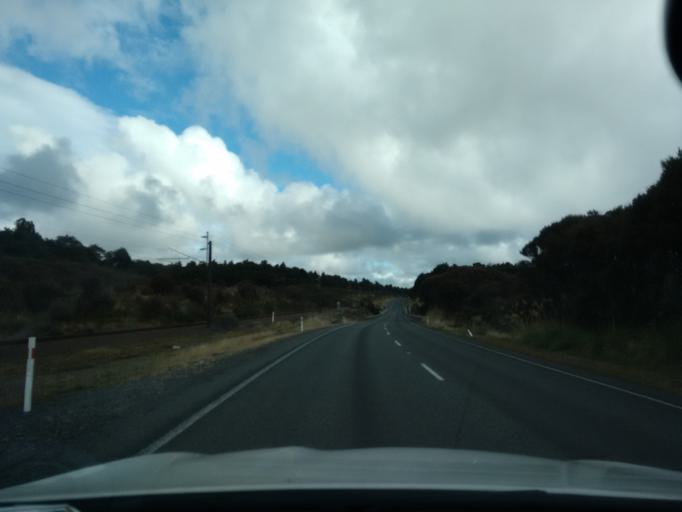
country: NZ
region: Manawatu-Wanganui
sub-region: Ruapehu District
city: Waiouru
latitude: -39.3029
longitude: 175.3898
